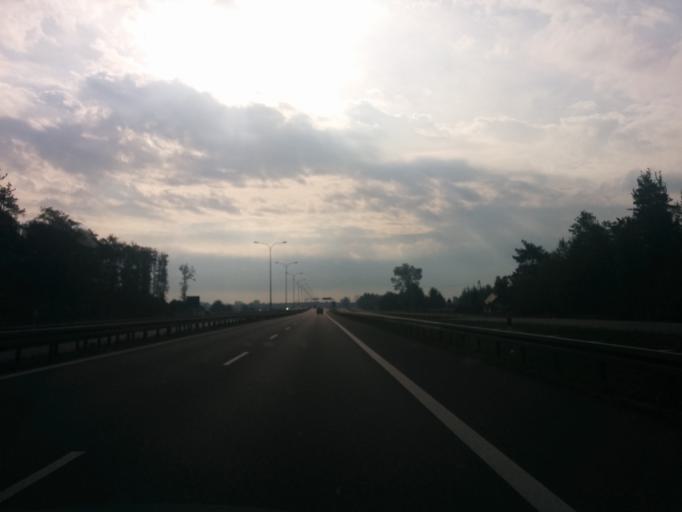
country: PL
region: Masovian Voivodeship
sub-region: Powiat bialobrzeski
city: Stara Blotnica
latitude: 51.5757
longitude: 21.0099
